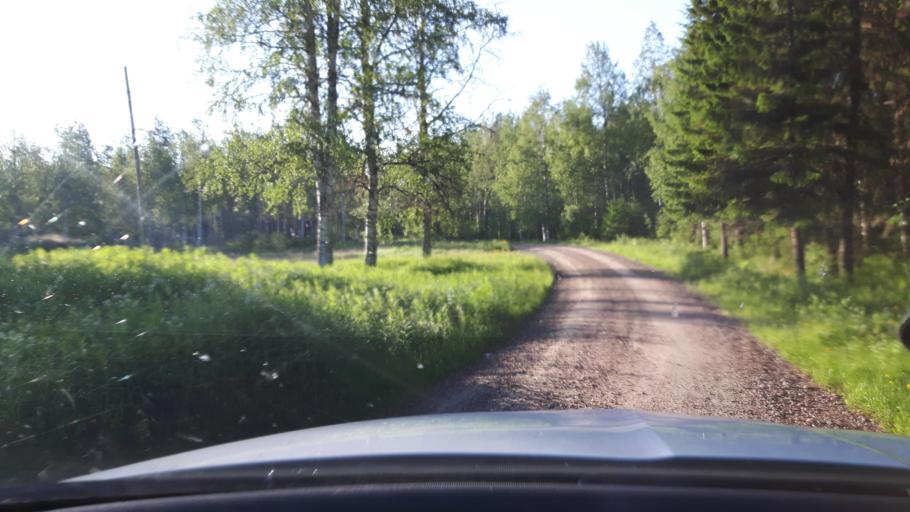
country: SE
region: Vaesternorrland
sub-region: Ange Kommun
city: Ange
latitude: 62.1823
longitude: 15.6292
